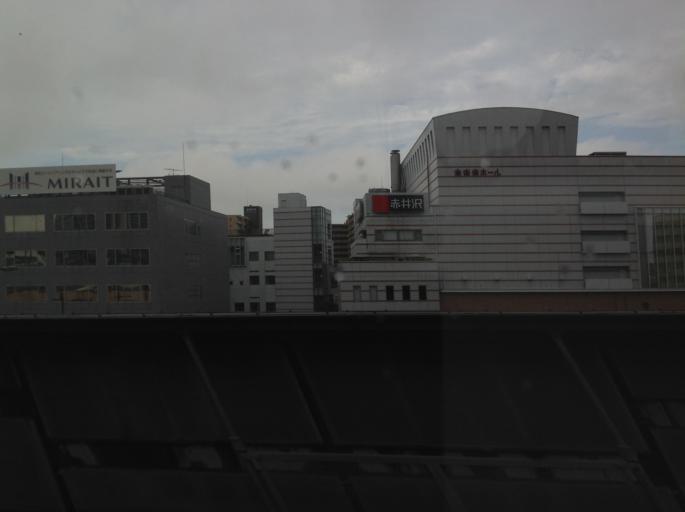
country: JP
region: Miyagi
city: Sendai
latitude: 38.2278
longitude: 140.8855
